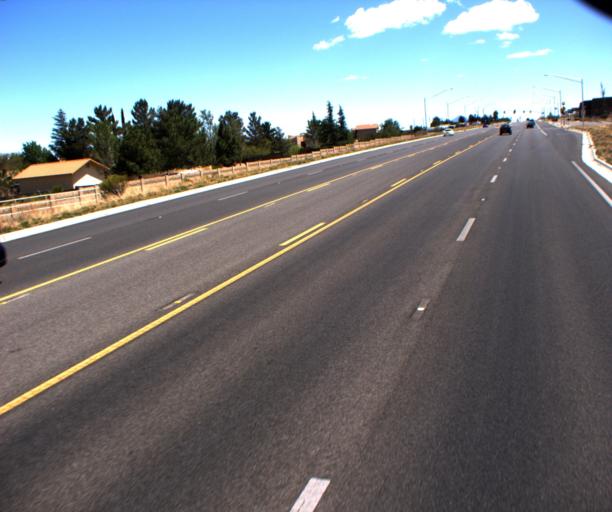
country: US
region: Arizona
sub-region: Cochise County
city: Sierra Vista Southeast
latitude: 31.4402
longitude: -110.2508
